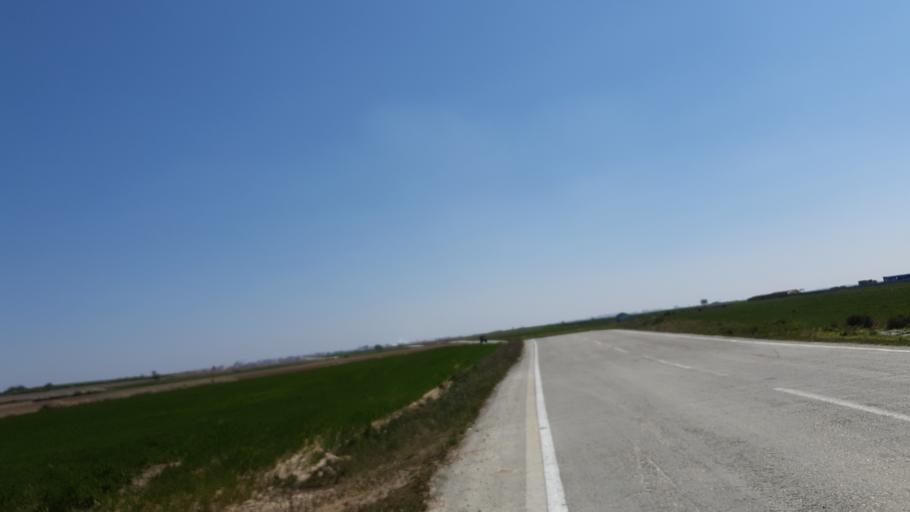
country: TR
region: Tekirdag
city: Cerkezkoey
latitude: 41.3255
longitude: 27.9266
